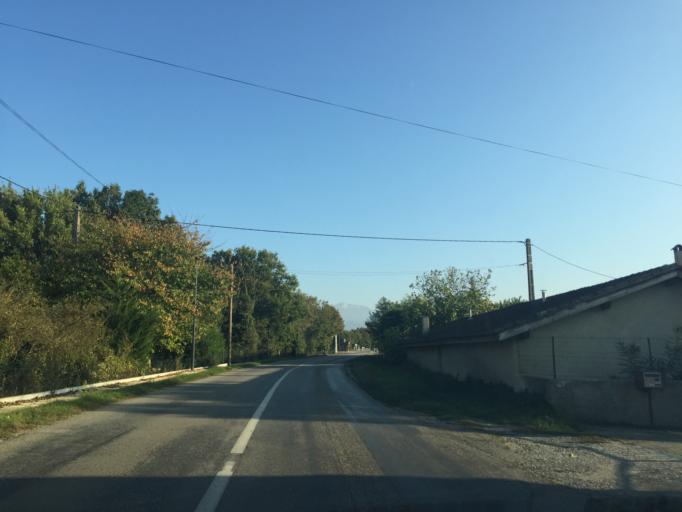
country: FR
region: Rhone-Alpes
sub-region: Departement de la Drome
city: Bourg-de-Peage
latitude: 45.0175
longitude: 5.0799
